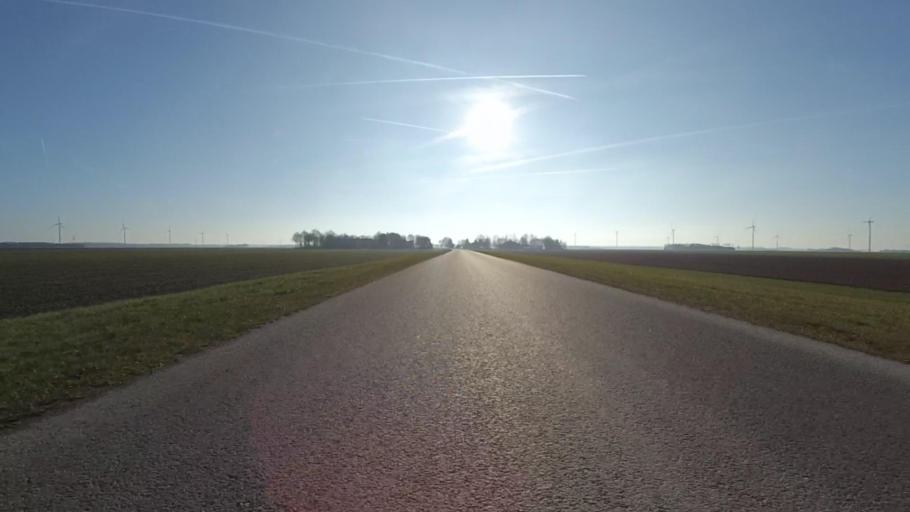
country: NL
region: Utrecht
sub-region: Gemeente Bunschoten
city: Bunschoten
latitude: 52.3057
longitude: 5.4201
